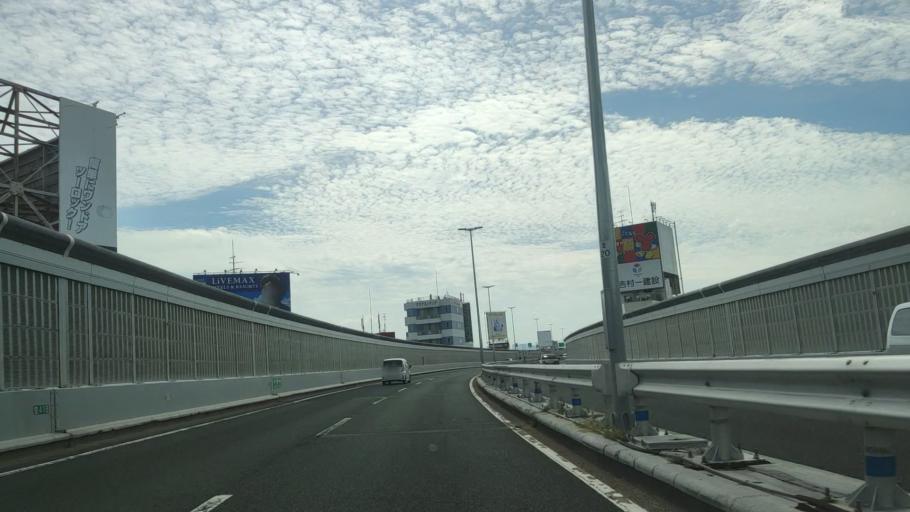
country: JP
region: Osaka
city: Toyonaka
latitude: 34.7778
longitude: 135.4570
